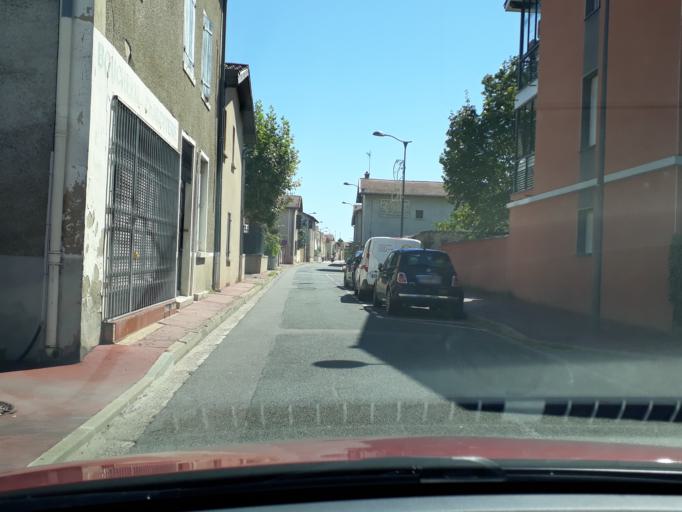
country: FR
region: Rhone-Alpes
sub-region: Departement du Rhone
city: Genas
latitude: 45.7015
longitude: 4.9778
